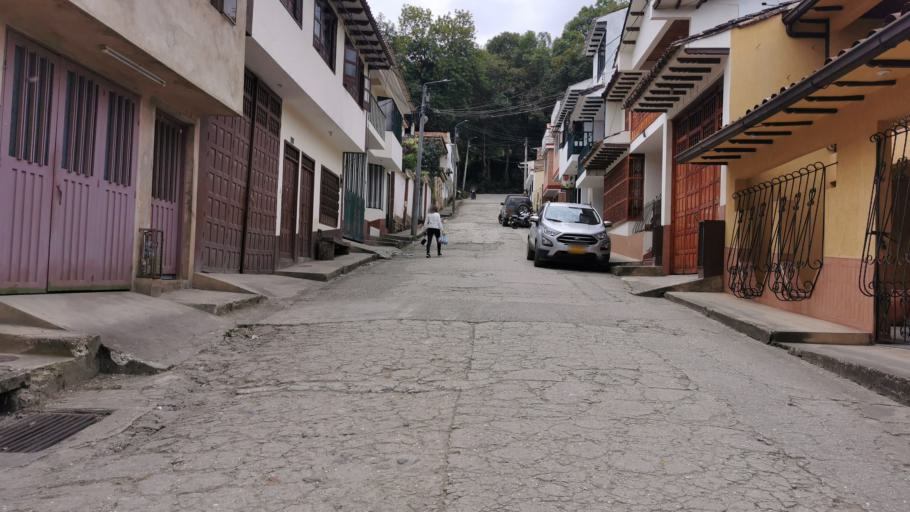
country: CO
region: Cundinamarca
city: Tenza
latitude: 5.0766
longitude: -73.4234
